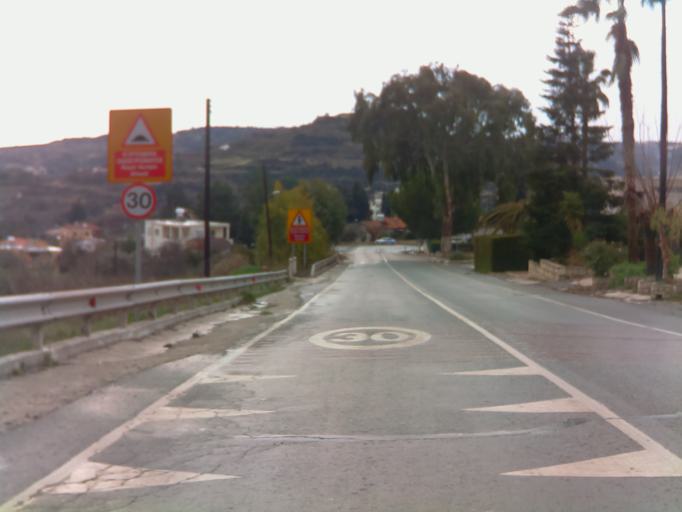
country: CY
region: Pafos
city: Tala
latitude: 34.8851
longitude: 32.4823
